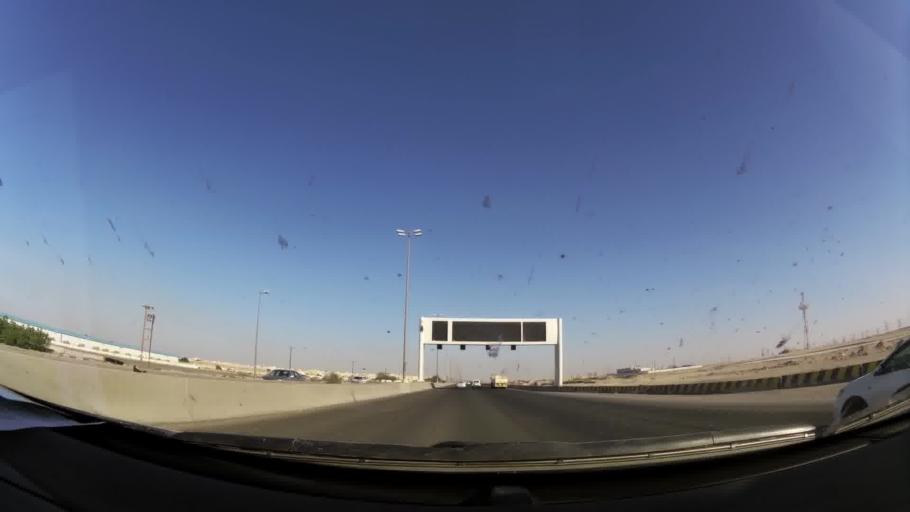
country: KW
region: Al Asimah
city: Ar Rabiyah
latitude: 29.2651
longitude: 47.8542
